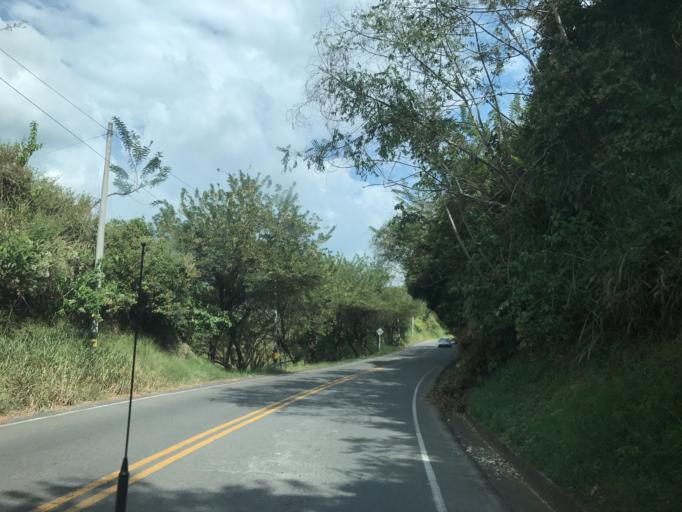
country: CO
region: Valle del Cauca
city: Cartago
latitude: 4.7261
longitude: -75.8889
